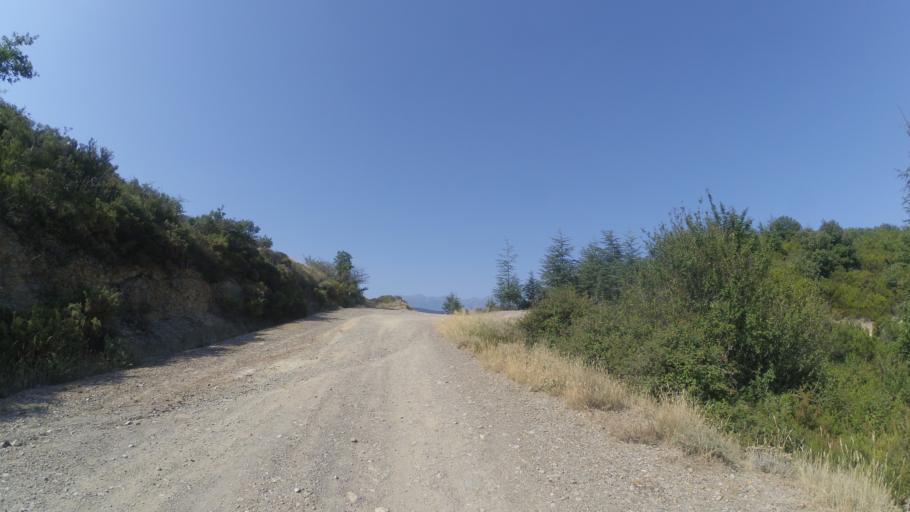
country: FR
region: Languedoc-Roussillon
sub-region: Departement des Pyrenees-Orientales
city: Millas
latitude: 42.6267
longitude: 2.6758
